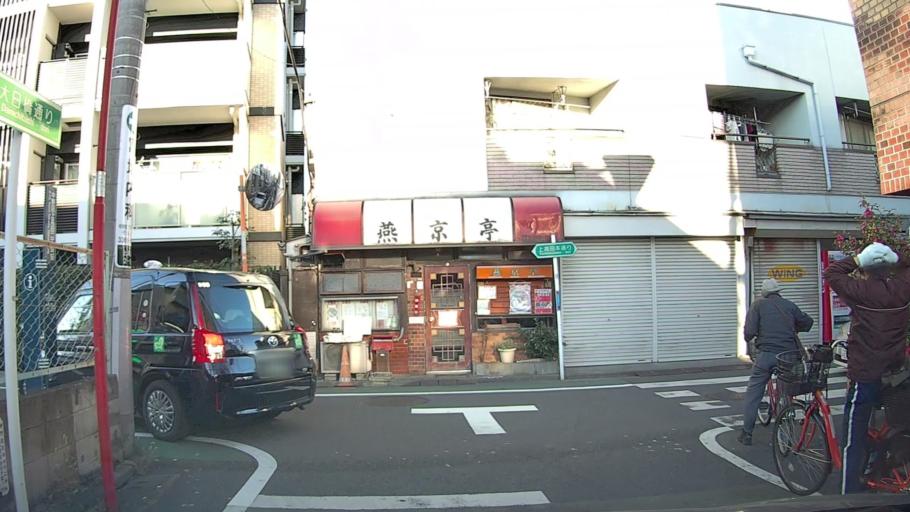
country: JP
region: Tokyo
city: Tokyo
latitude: 35.7127
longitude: 139.6741
